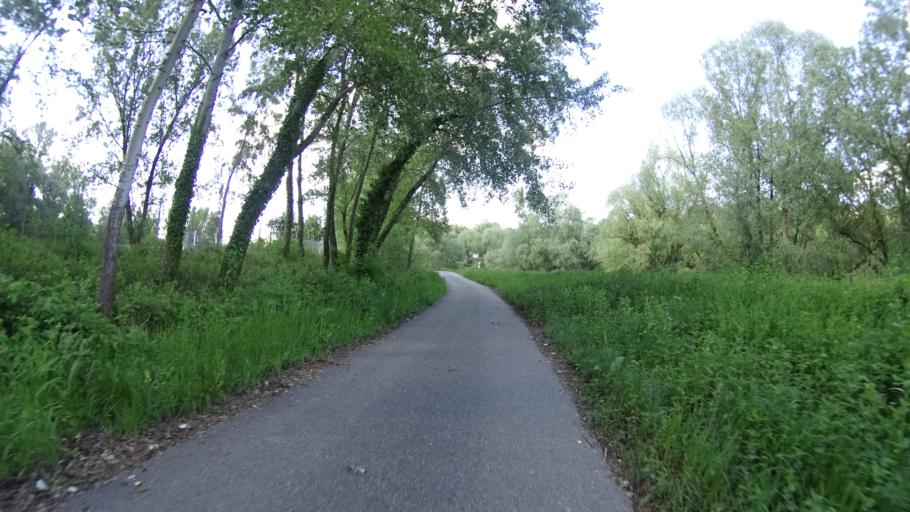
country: DE
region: Rheinland-Pfalz
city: Neupotz
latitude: 49.0676
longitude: 8.3449
